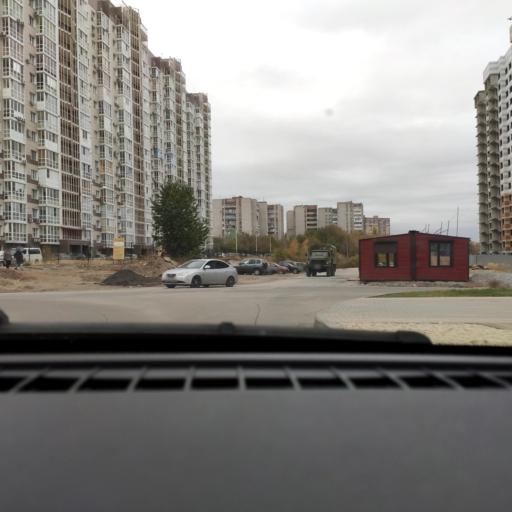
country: RU
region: Voronezj
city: Voronezh
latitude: 51.7142
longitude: 39.2697
